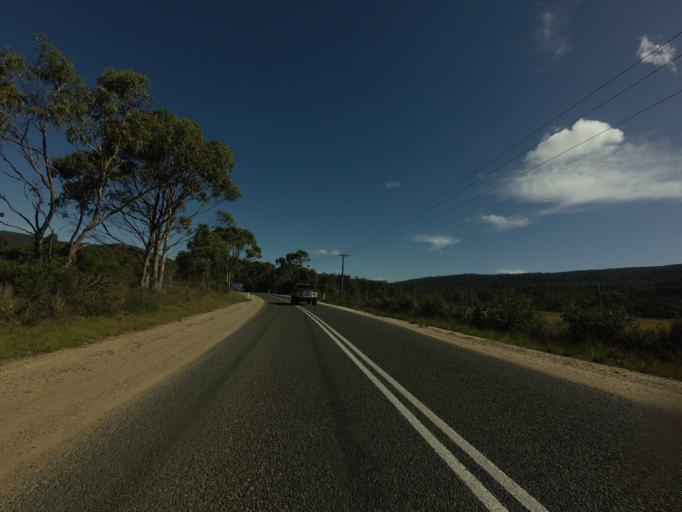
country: AU
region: Tasmania
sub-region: Break O'Day
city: St Helens
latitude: -41.8347
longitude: 148.2549
